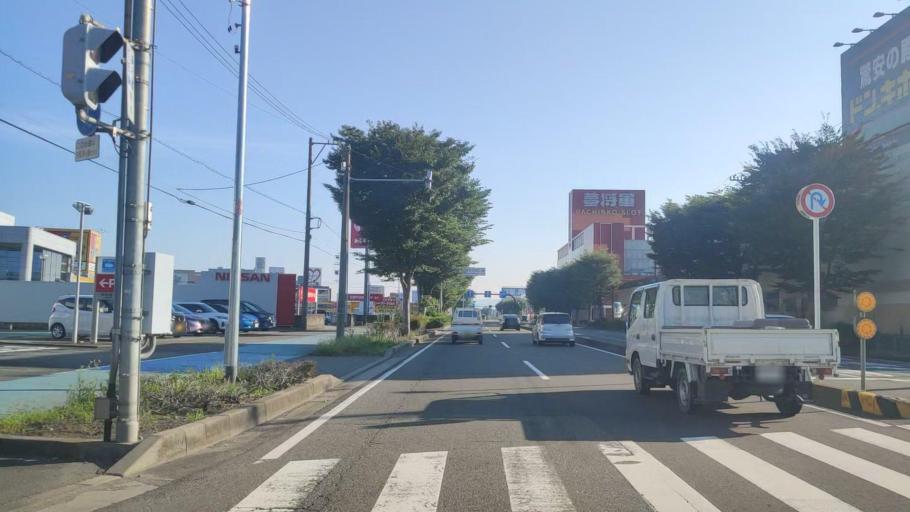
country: JP
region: Fukui
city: Fukui-shi
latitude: 36.0926
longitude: 136.2503
